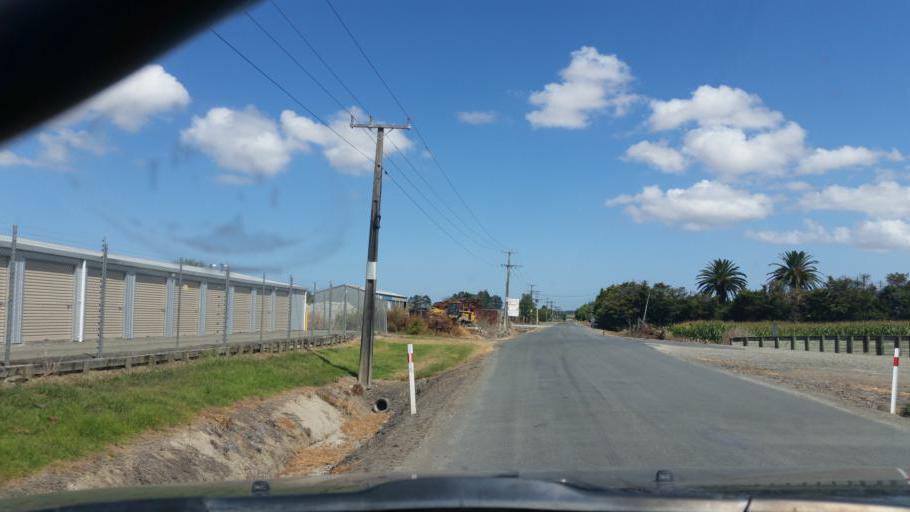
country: NZ
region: Northland
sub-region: Kaipara District
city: Dargaville
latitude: -35.9443
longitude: 173.8620
